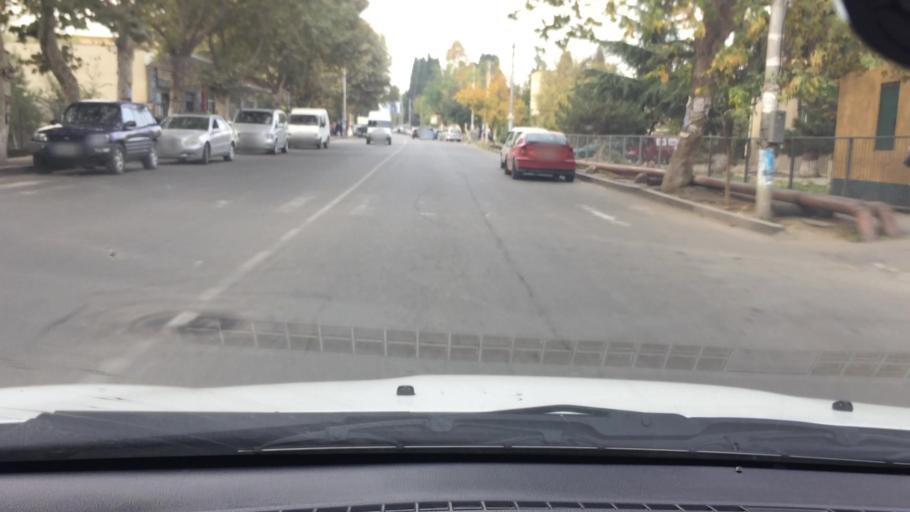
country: GE
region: Kvemo Kartli
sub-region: Marneuli
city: Marneuli
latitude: 41.4703
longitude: 44.8165
